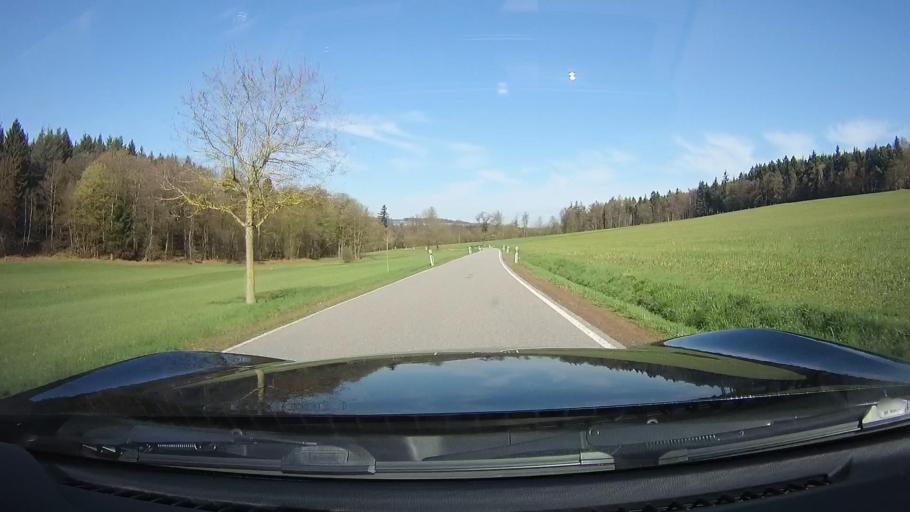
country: DE
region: Baden-Wuerttemberg
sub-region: Karlsruhe Region
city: Neunkirchen
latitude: 49.4064
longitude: 8.9689
